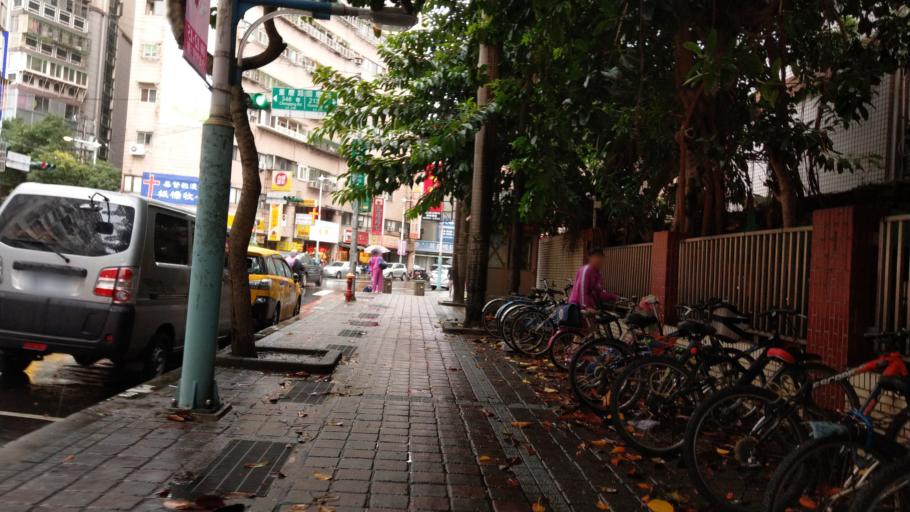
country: TW
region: Taipei
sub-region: Taipei
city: Banqiao
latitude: 24.9976
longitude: 121.4634
